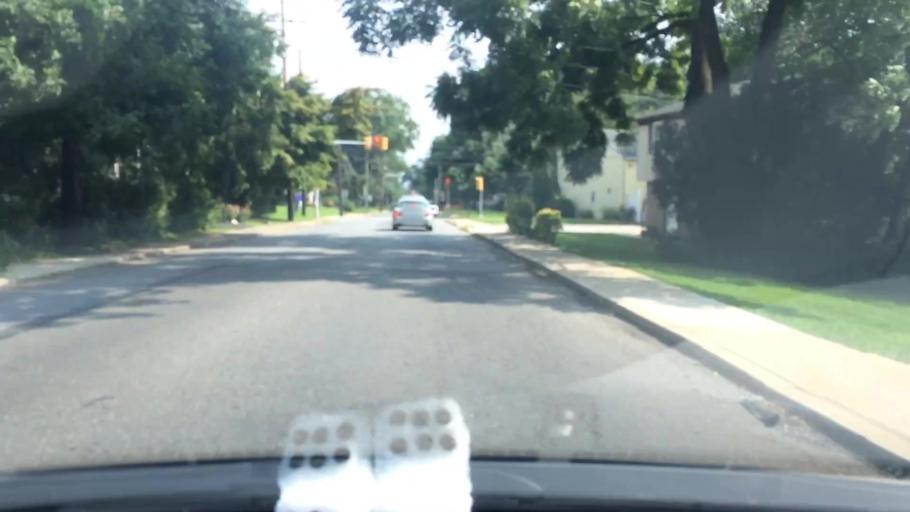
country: US
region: Pennsylvania
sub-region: Delaware County
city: Morton
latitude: 39.9089
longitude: -75.3237
